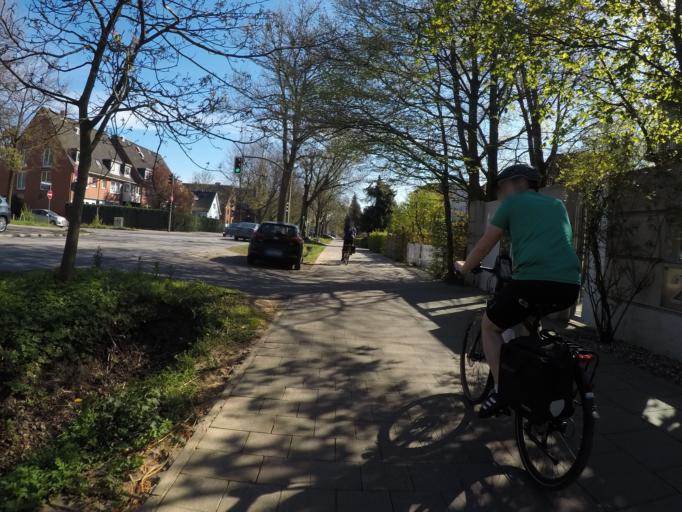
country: DE
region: Hamburg
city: Eidelstedt
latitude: 53.6292
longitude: 9.9100
